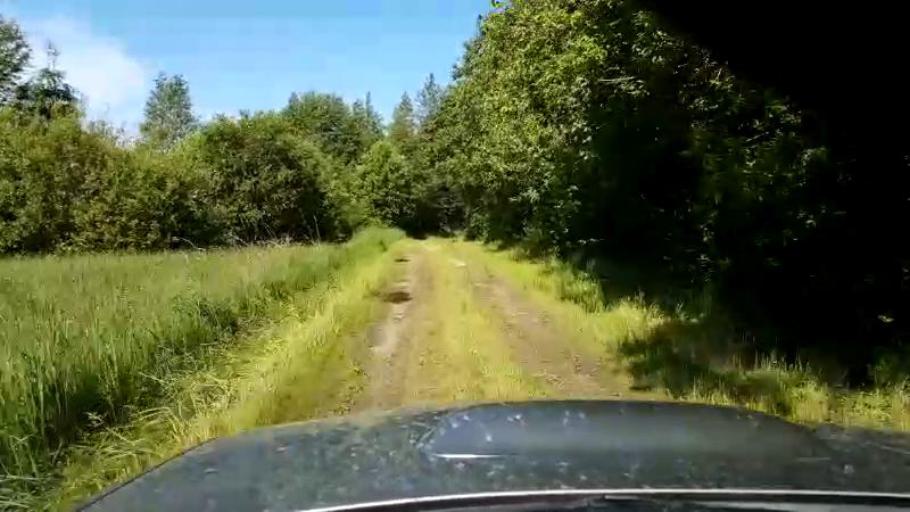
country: EE
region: Paernumaa
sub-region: Sindi linn
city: Sindi
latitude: 58.4976
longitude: 24.7039
